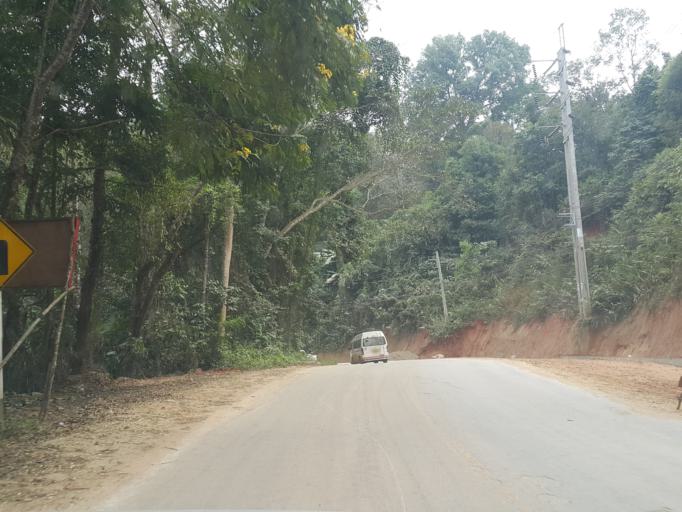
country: TH
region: Chiang Mai
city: Mae Taeng
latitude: 19.1207
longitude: 98.7116
